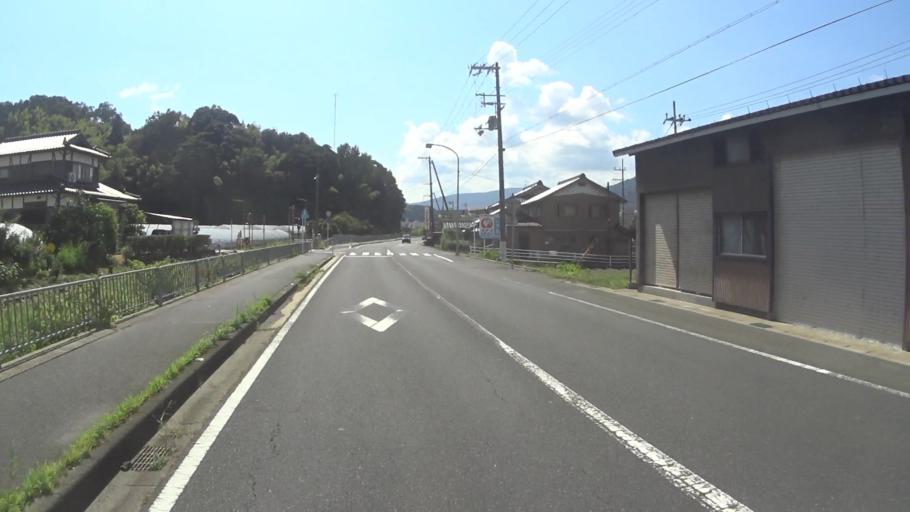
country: JP
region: Kyoto
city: Miyazu
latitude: 35.5412
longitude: 135.2086
